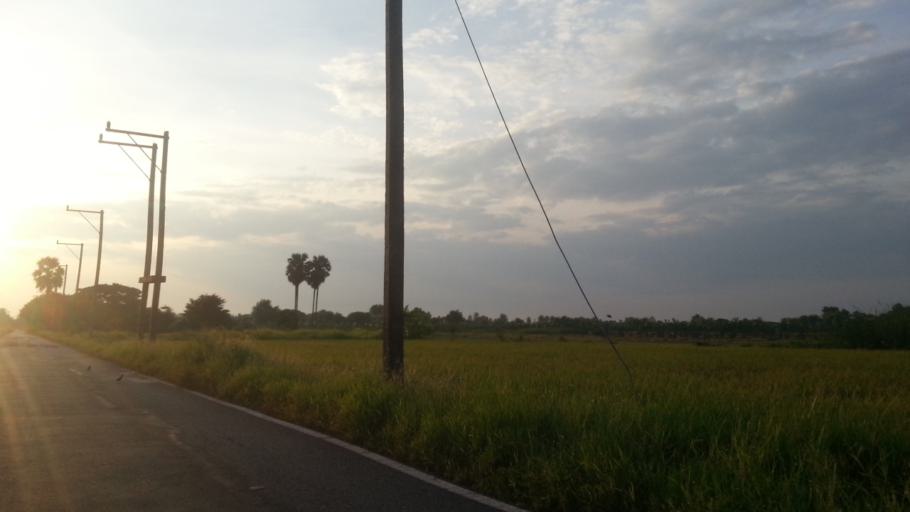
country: TH
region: Pathum Thani
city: Ban Rangsit
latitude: 14.0411
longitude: 100.8528
